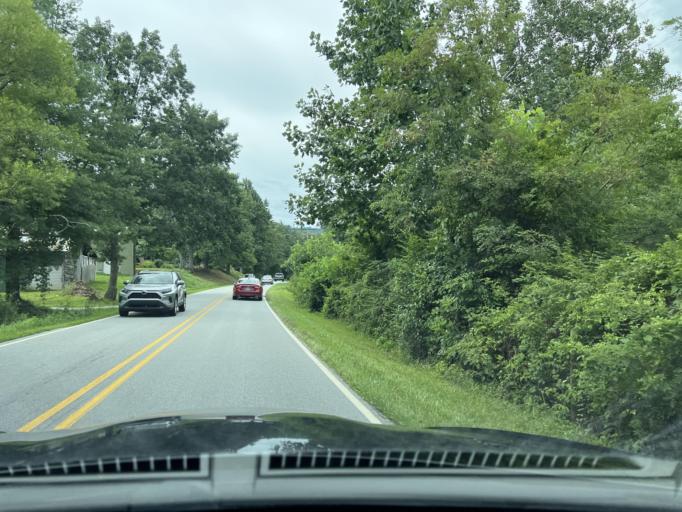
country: US
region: North Carolina
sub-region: Henderson County
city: Fruitland
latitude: 35.4079
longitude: -82.4094
